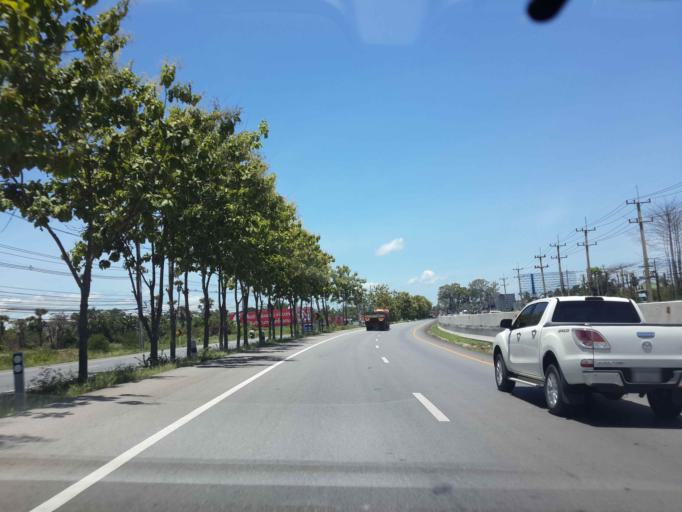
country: TH
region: Phetchaburi
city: Phetchaburi
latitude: 13.1368
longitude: 99.8591
